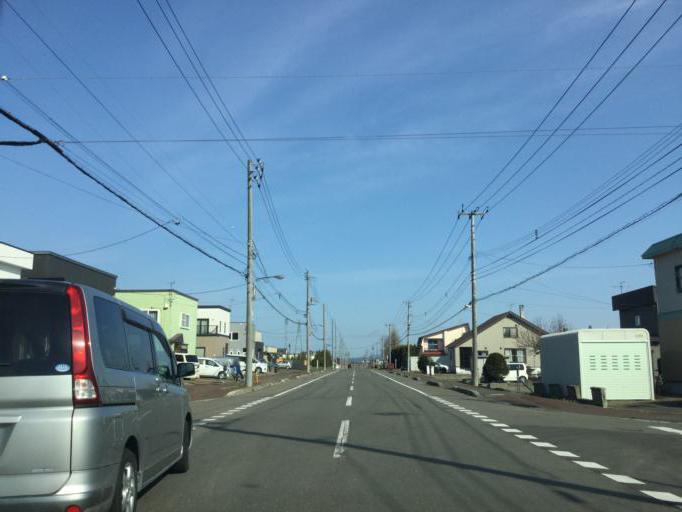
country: JP
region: Hokkaido
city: Ebetsu
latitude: 43.1500
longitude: 141.6492
